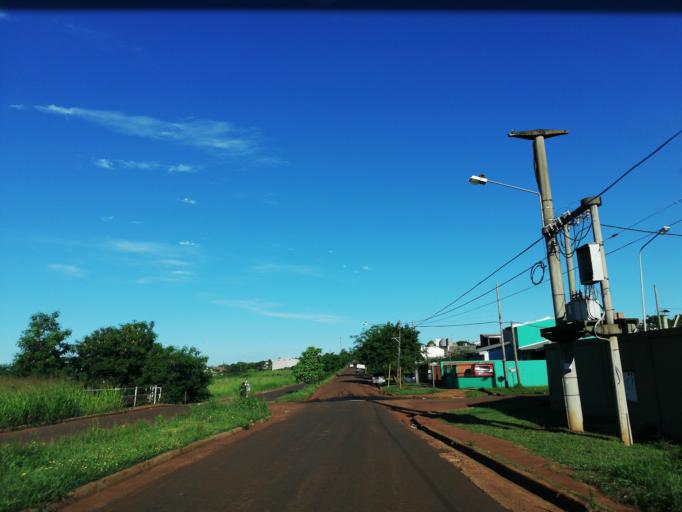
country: AR
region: Misiones
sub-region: Departamento de Capital
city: Posadas
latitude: -27.4353
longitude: -55.9202
